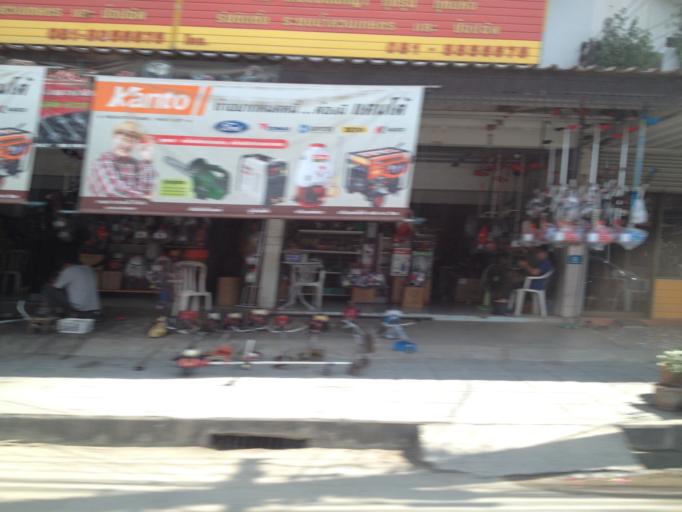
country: TH
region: Chiang Mai
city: Hang Dong
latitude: 18.6985
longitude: 98.9290
